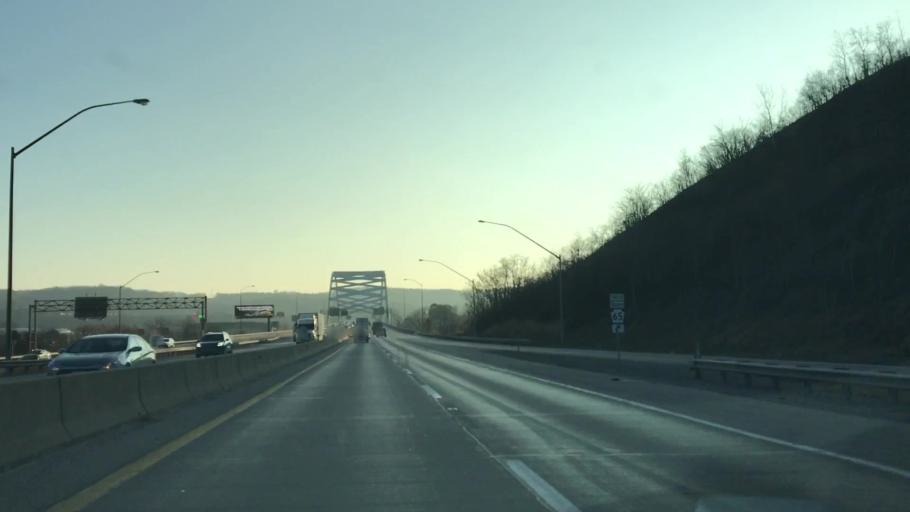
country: US
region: Pennsylvania
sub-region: Allegheny County
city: Coraopolis
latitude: 40.5205
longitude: -80.1323
